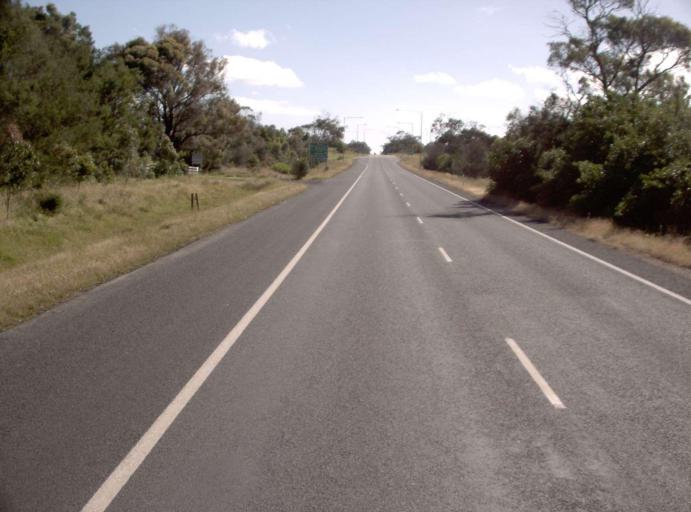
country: AU
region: Victoria
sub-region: Bass Coast
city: North Wonthaggi
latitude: -38.4312
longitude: 145.5010
